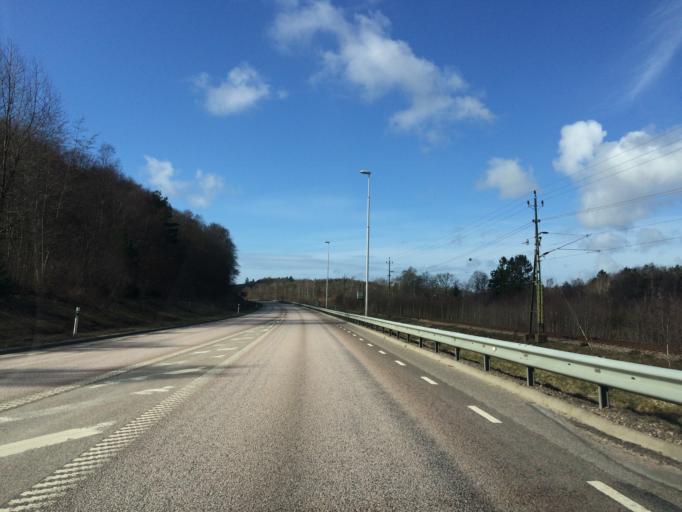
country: SE
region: Halland
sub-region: Laholms Kommun
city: Knared
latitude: 56.5156
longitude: 13.3103
